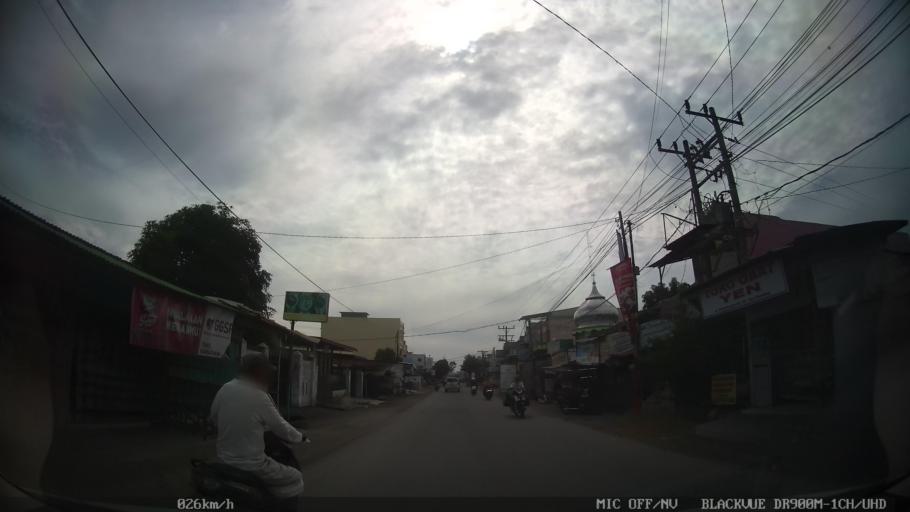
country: ID
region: North Sumatra
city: Medan
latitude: 3.6203
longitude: 98.7383
